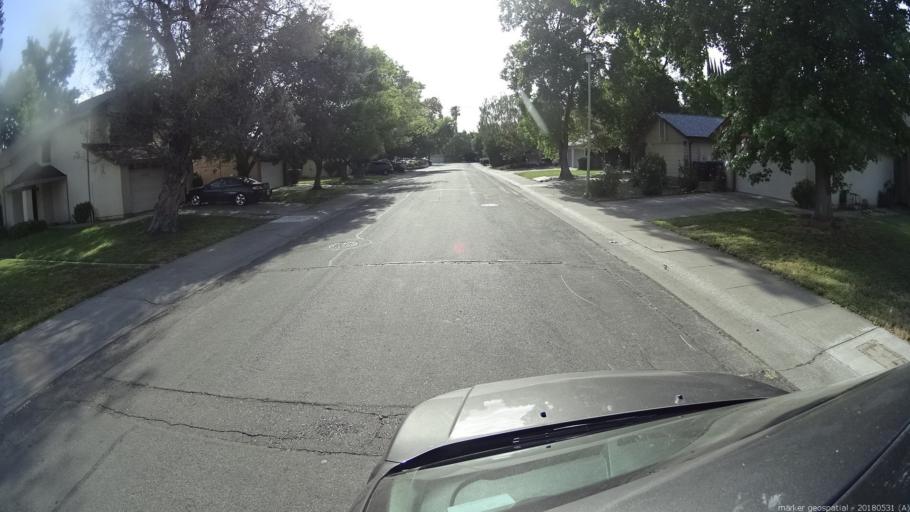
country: US
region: California
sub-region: Sacramento County
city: Sacramento
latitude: 38.6297
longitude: -121.4867
